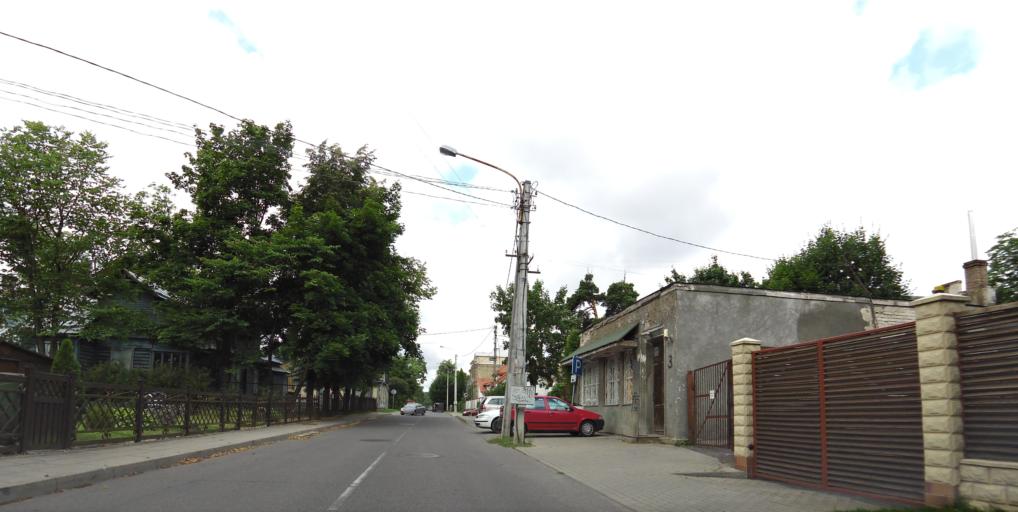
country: LT
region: Vilnius County
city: Seskine
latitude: 54.6938
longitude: 25.2569
